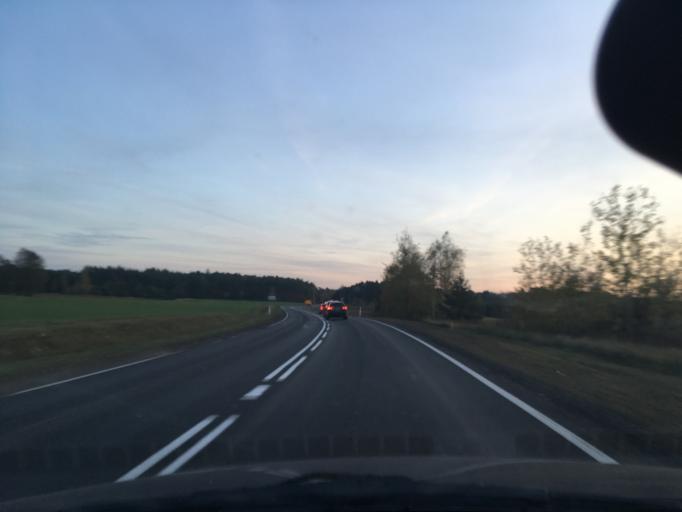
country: PL
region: Masovian Voivodeship
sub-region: Powiat plocki
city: Wyszogrod
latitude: 52.3522
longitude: 20.2089
